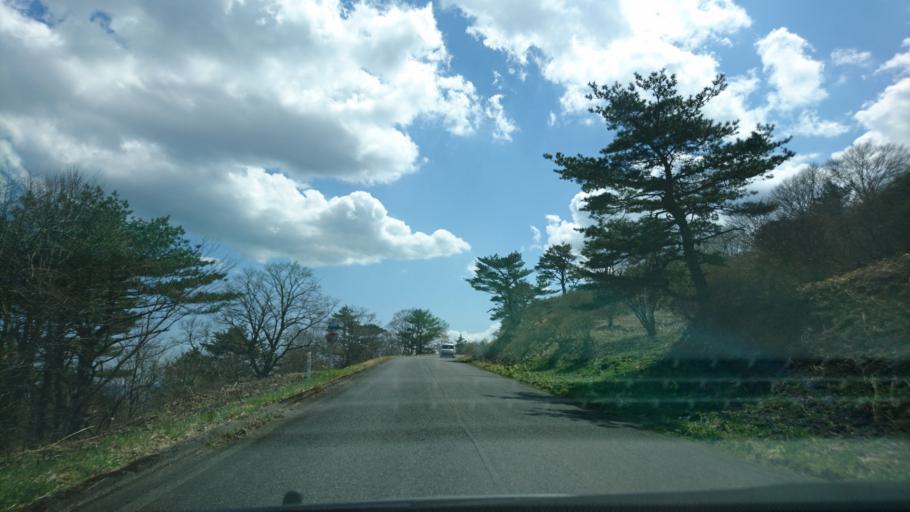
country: JP
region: Iwate
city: Ofunato
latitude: 38.9742
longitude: 141.4536
